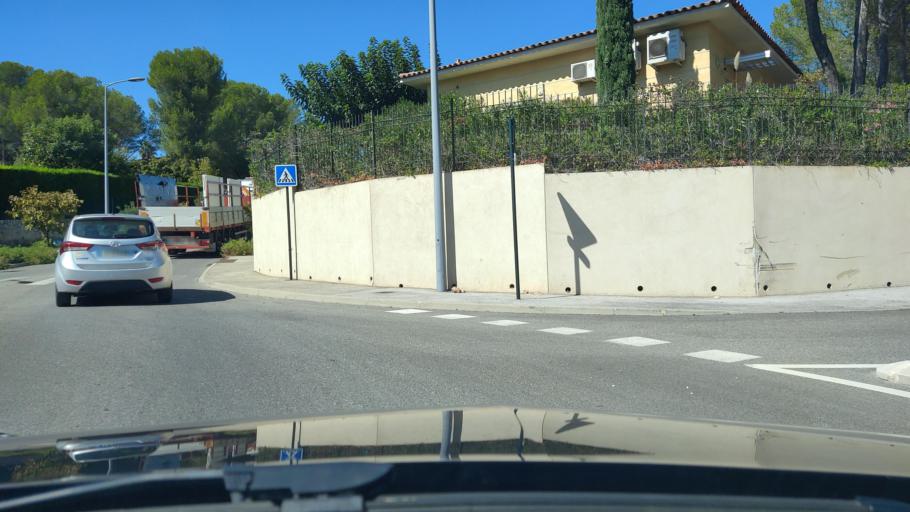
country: FR
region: Provence-Alpes-Cote d'Azur
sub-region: Departement du Var
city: Sanary-sur-Mer
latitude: 43.1402
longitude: 5.7817
